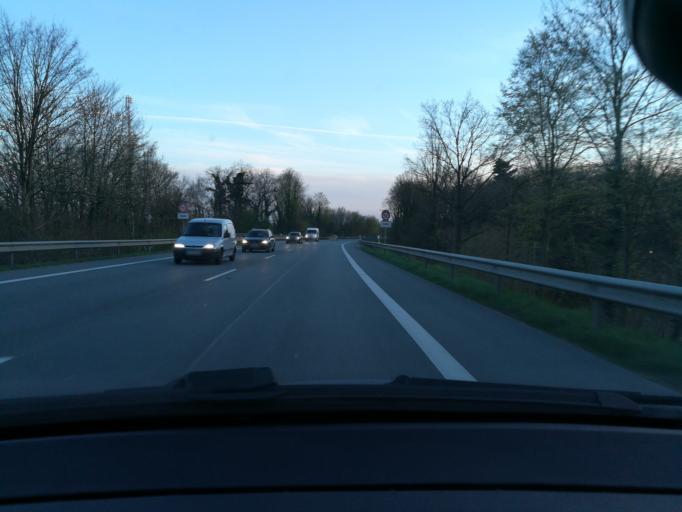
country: DE
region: North Rhine-Westphalia
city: Halle
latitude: 52.0615
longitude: 8.3475
